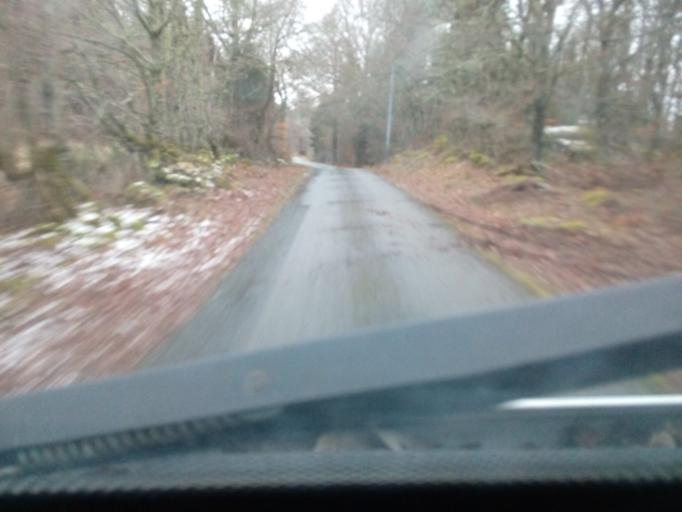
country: FR
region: Limousin
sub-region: Departement de la Creuse
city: Felletin
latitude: 45.8248
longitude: 2.2528
